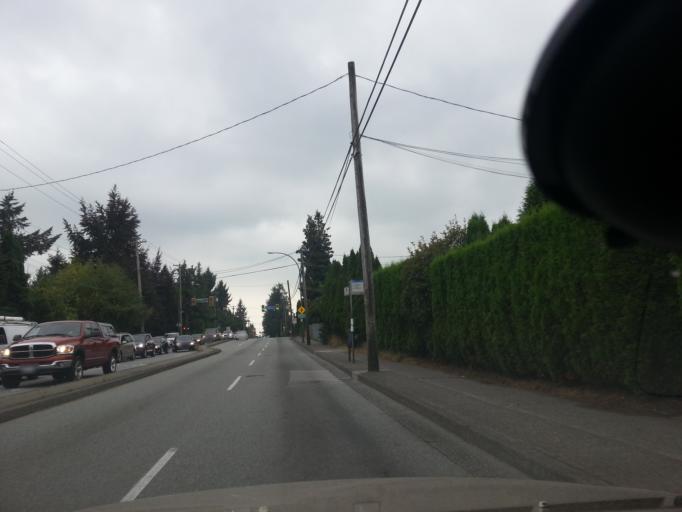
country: CA
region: British Columbia
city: Port Moody
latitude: 49.2699
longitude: -122.8796
